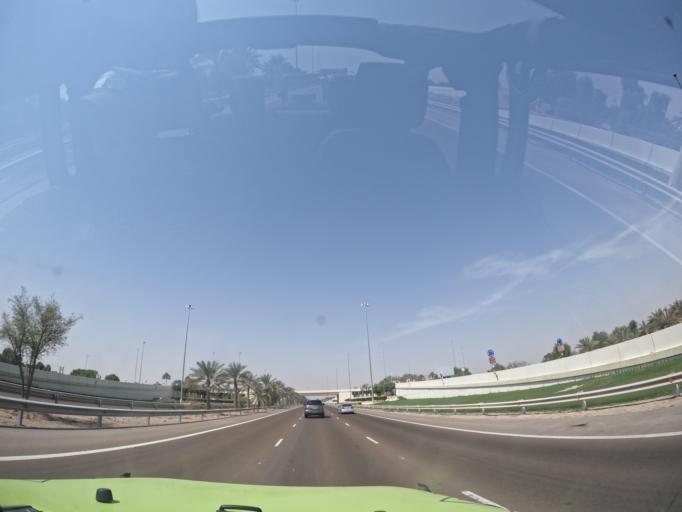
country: AE
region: Abu Dhabi
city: Al Ain
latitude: 24.1704
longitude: 55.1034
